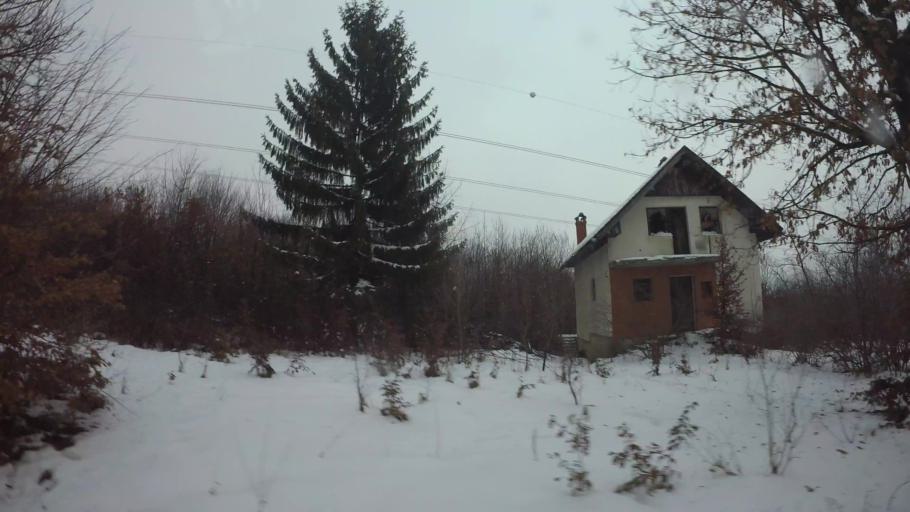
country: BA
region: Federation of Bosnia and Herzegovina
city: Hadzici
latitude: 43.8436
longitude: 18.2680
